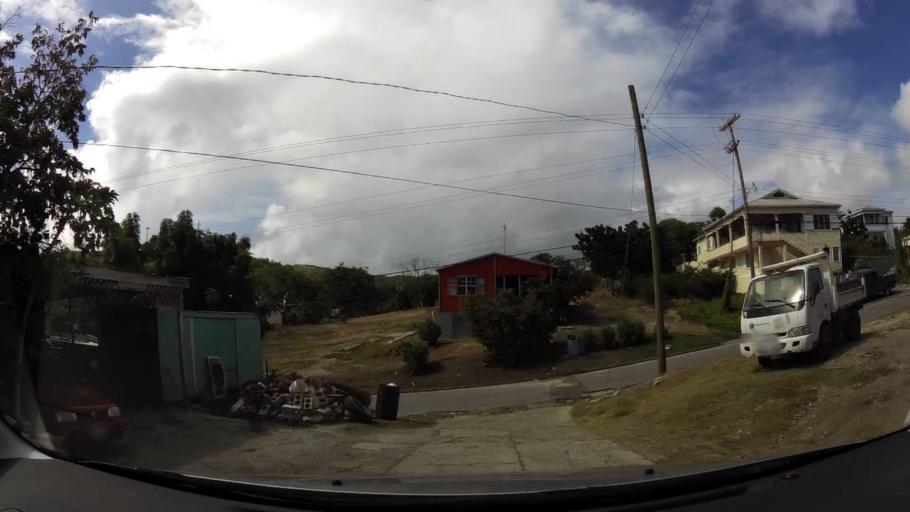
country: AG
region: Saint Paul
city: Liberta
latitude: 17.0430
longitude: -61.7512
